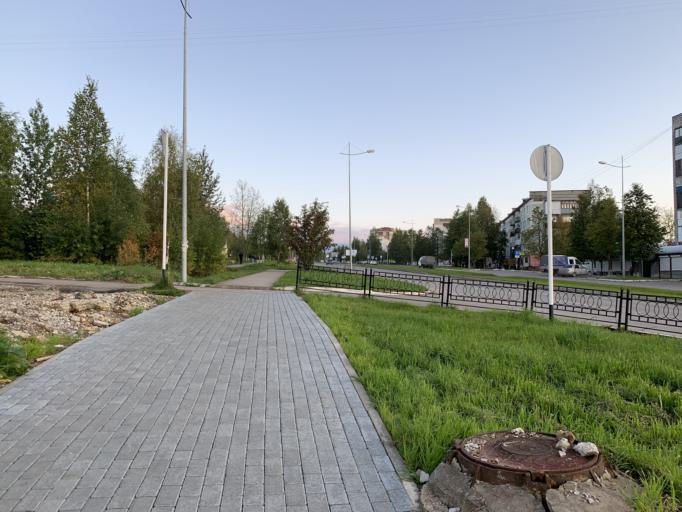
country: RU
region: Perm
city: Gubakha
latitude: 58.8355
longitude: 57.5559
